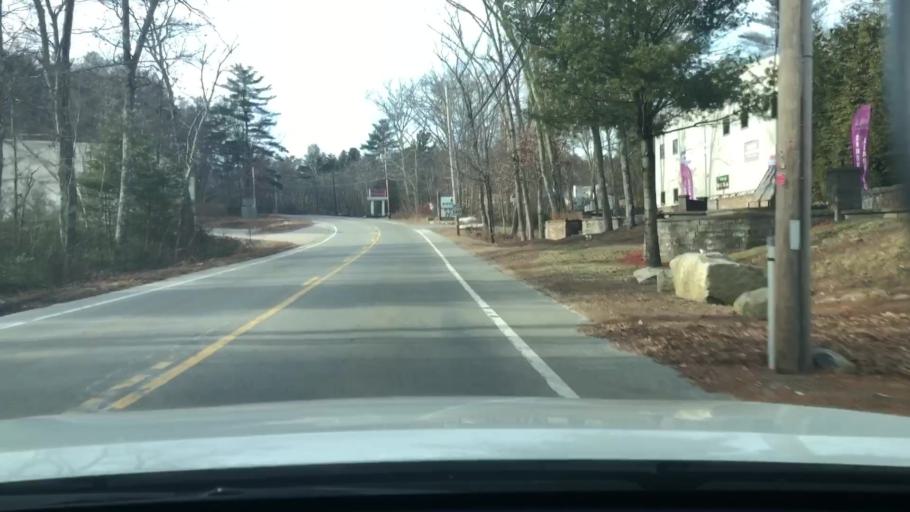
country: US
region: Massachusetts
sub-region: Worcester County
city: Hopedale
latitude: 42.1551
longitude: -71.5690
